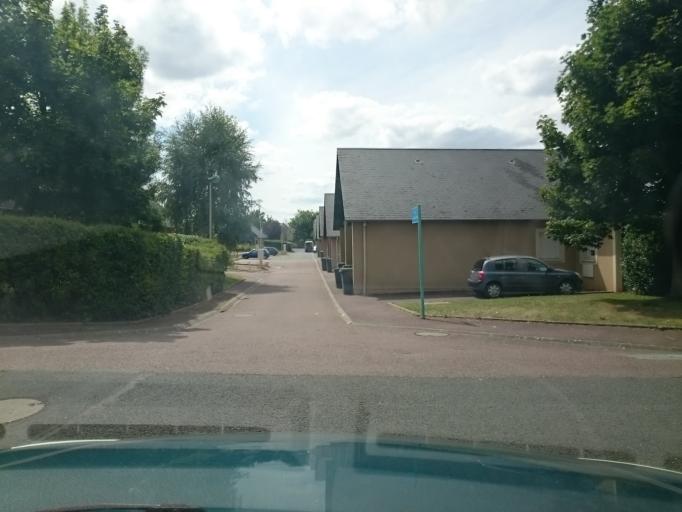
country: FR
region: Lower Normandy
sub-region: Departement du Calvados
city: Ifs
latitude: 49.1365
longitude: -0.3466
